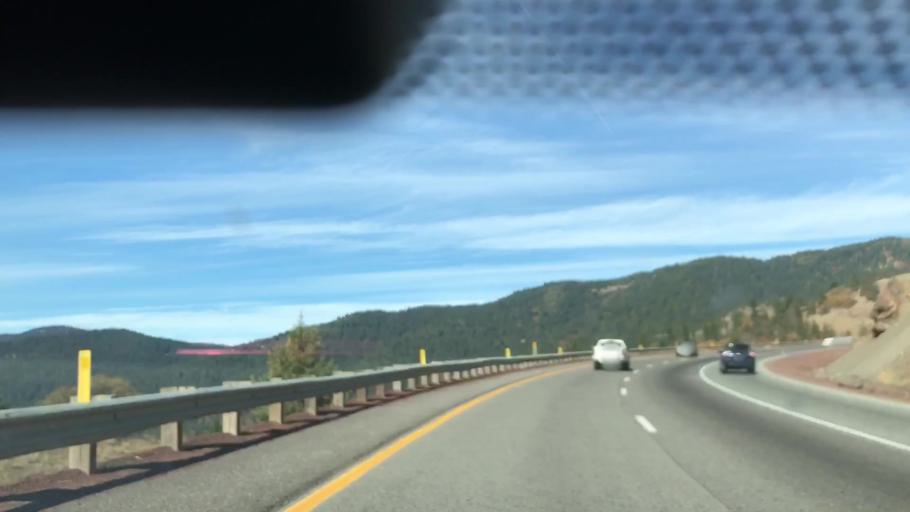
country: US
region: Oregon
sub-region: Jackson County
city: Ashland
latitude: 42.0526
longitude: -122.6095
